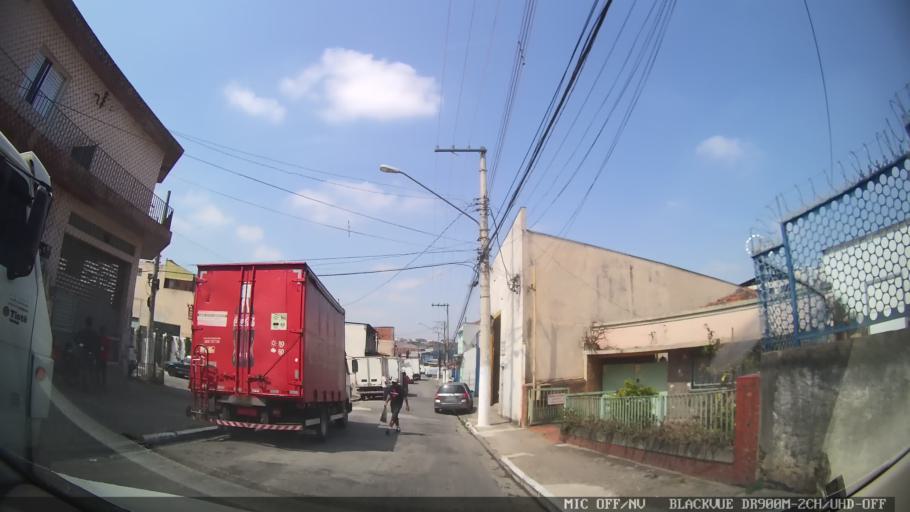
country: BR
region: Sao Paulo
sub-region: Sao Paulo
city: Sao Paulo
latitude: -23.4979
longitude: -46.6647
